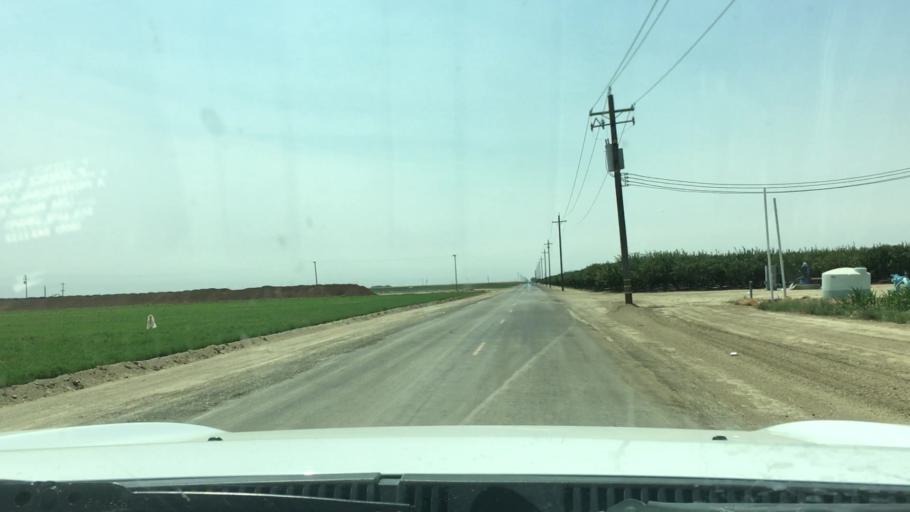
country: US
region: California
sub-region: Kern County
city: Wasco
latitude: 35.7271
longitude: -119.4371
